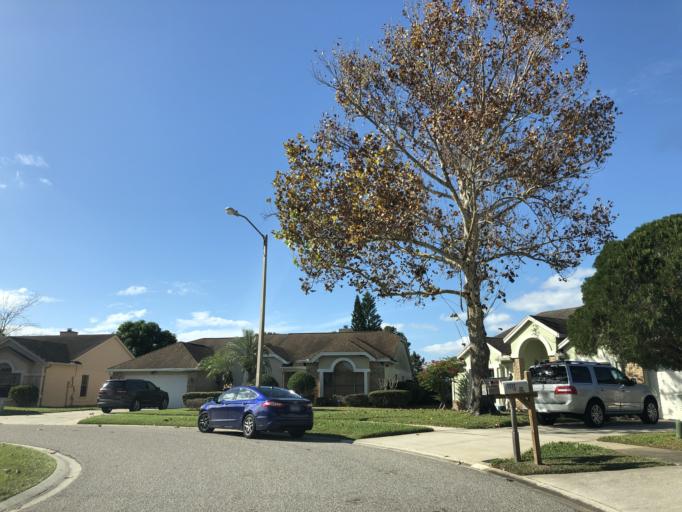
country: US
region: Florida
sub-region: Orange County
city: Hunters Creek
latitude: 28.3783
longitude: -81.4080
